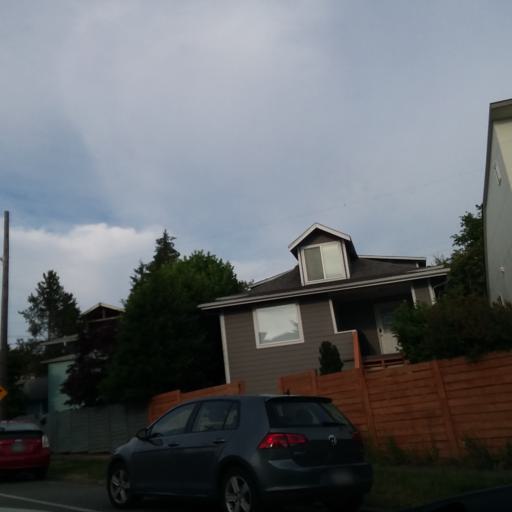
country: US
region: Washington
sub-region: King County
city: Seattle
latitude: 47.5803
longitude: -122.3930
